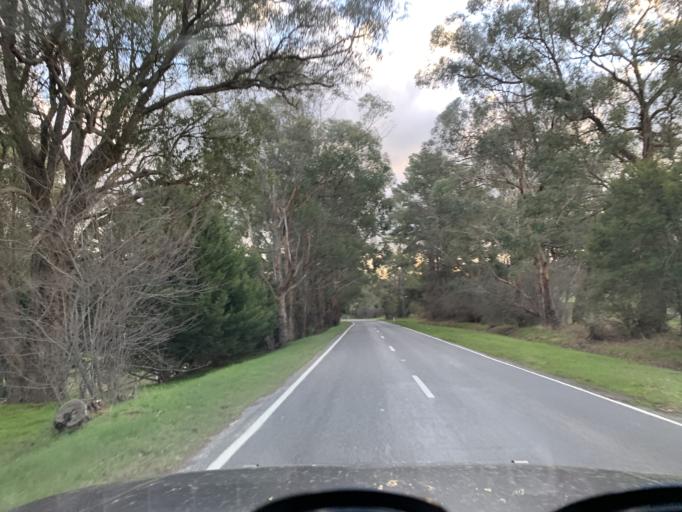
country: AU
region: Victoria
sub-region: Yarra Ranges
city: Woori Yallock
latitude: -37.7848
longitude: 145.5277
